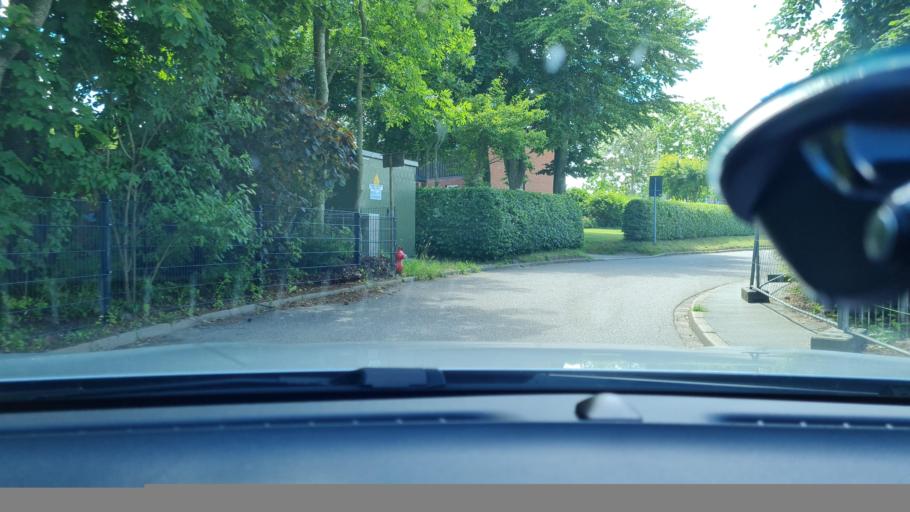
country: DE
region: Schleswig-Holstein
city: Rabenkirchen-Fauluck
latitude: 54.5933
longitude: 9.8672
